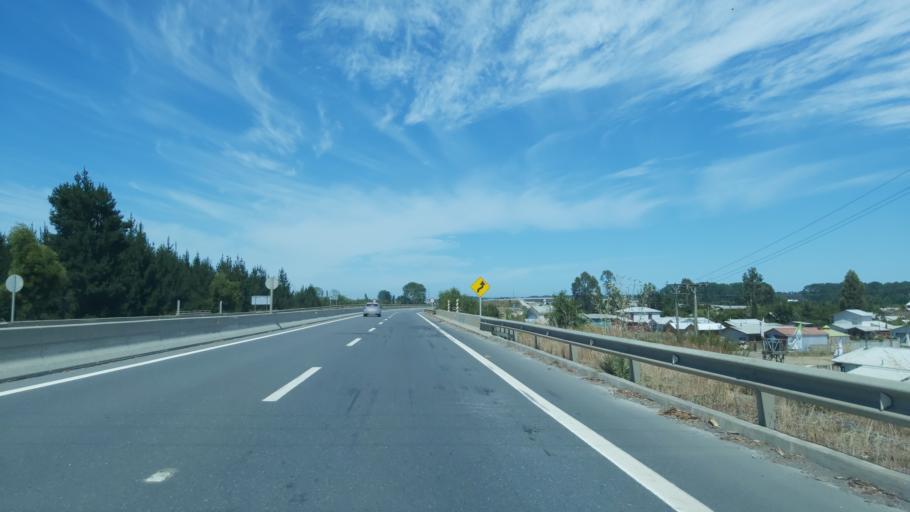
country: CL
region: Biobio
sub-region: Provincia de Concepcion
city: Lota
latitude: -37.1841
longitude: -73.1877
